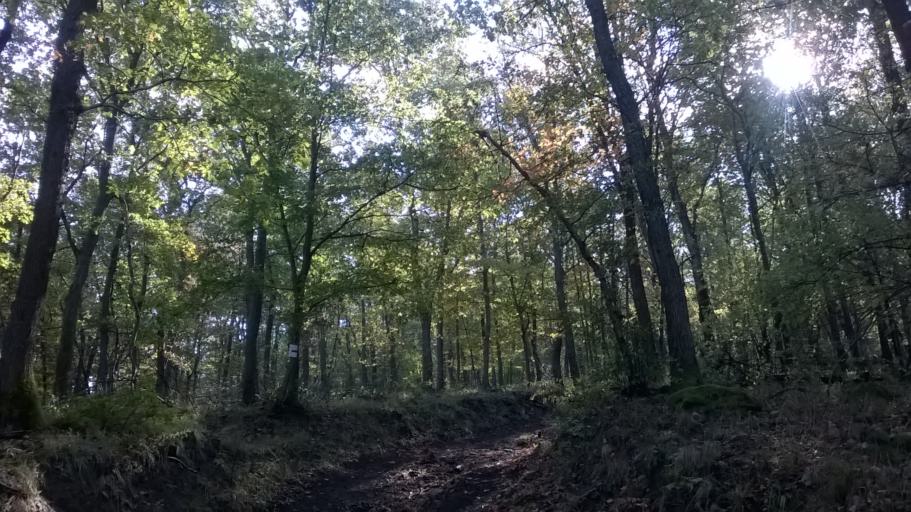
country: HU
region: Pest
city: Visegrad
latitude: 47.7852
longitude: 18.9987
